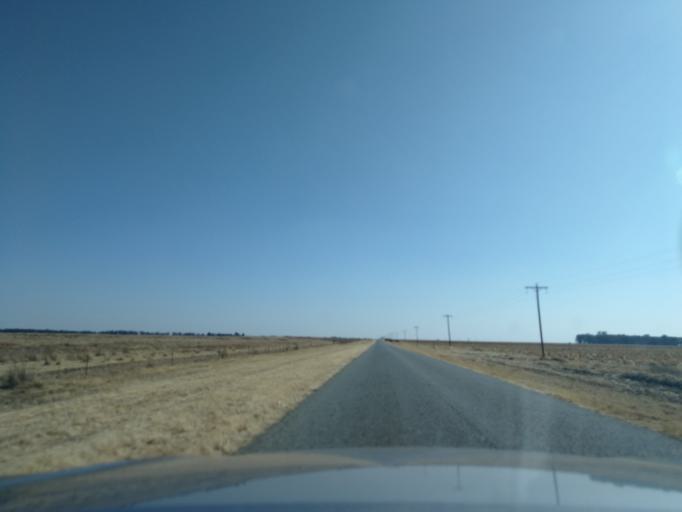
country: ZA
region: Orange Free State
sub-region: Fezile Dabi District Municipality
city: Viljoenskroon
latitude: -27.0792
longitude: 26.8504
